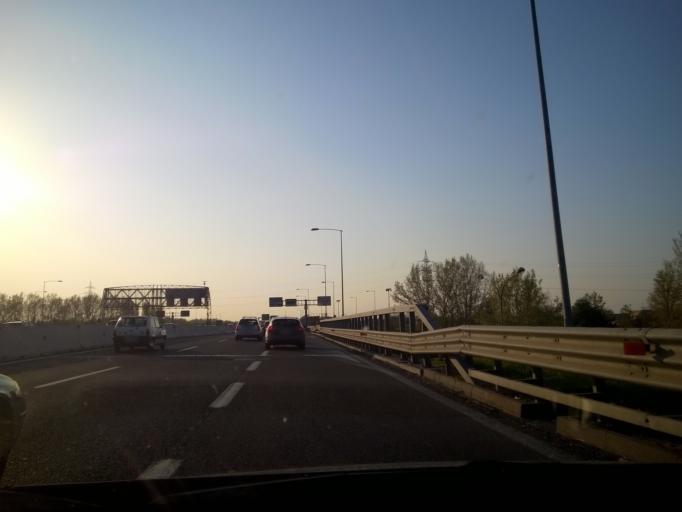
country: IT
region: Emilia-Romagna
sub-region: Provincia di Bologna
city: Bologna
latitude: 44.5230
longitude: 11.3640
